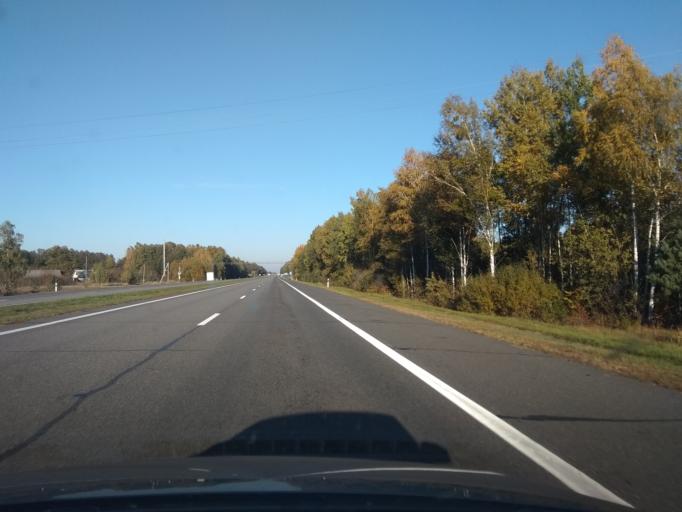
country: BY
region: Brest
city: Ivatsevichy
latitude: 52.6813
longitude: 25.3298
